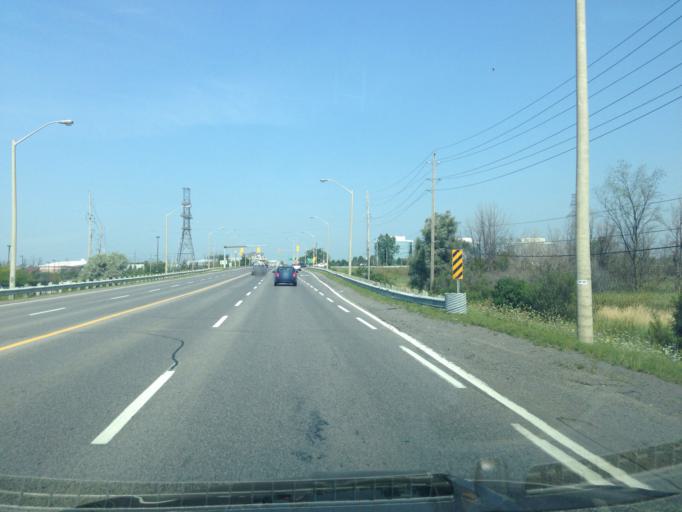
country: CA
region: Ontario
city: Ottawa
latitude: 45.4289
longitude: -75.6021
